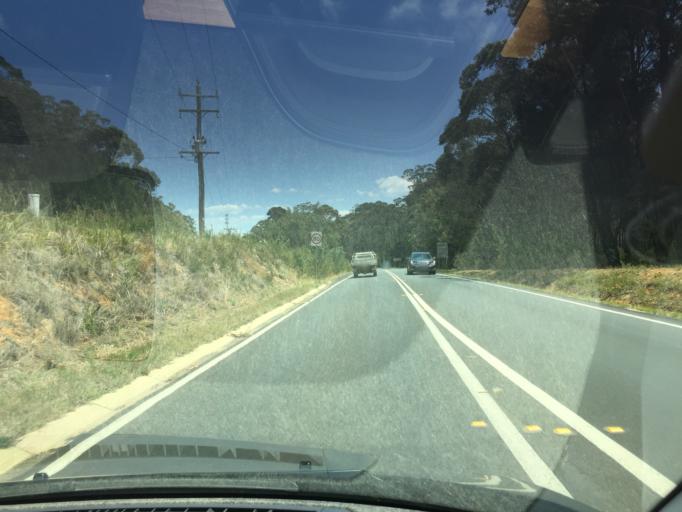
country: AU
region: New South Wales
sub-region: Bega Valley
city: Merimbula
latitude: -36.8663
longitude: 149.9041
